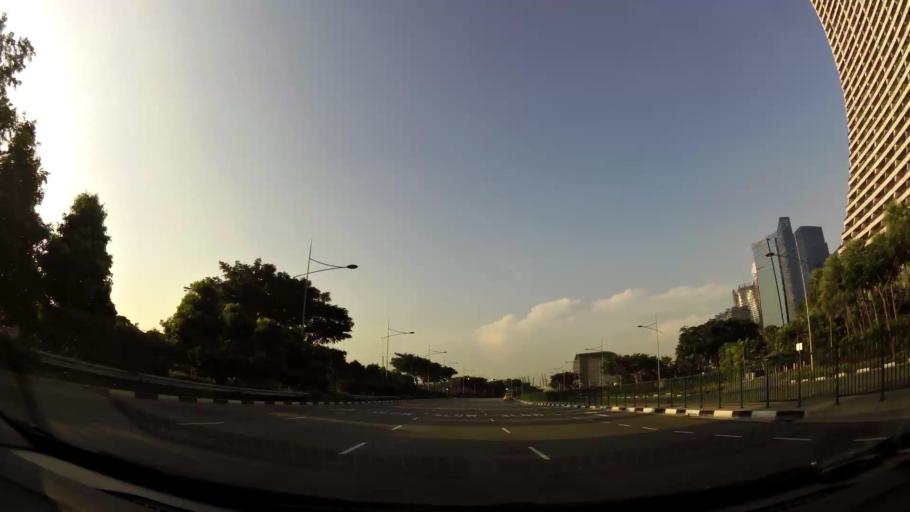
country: SG
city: Singapore
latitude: 1.2824
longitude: 103.8611
